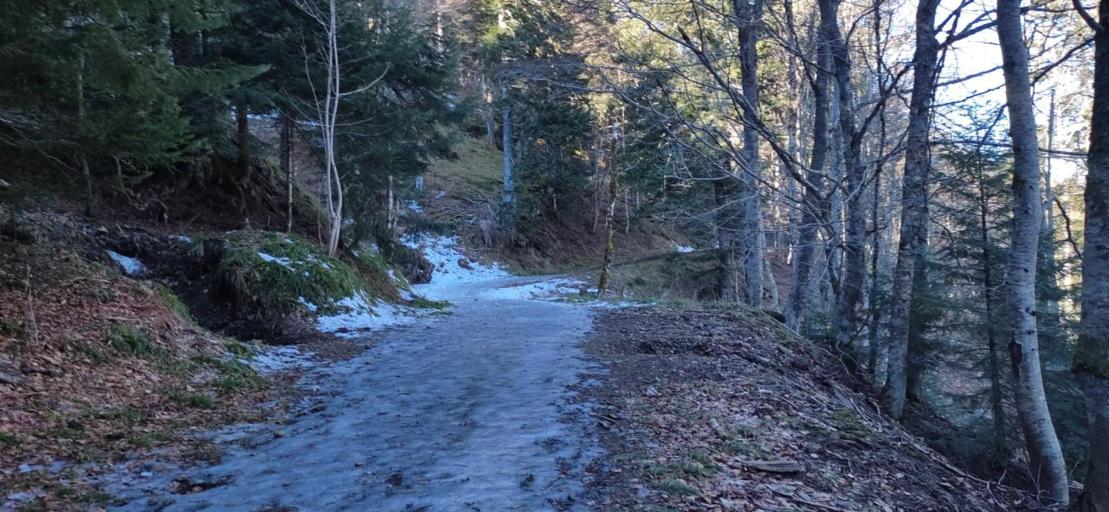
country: FR
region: Auvergne
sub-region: Departement du Puy-de-Dome
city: Mont-Dore
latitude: 45.5602
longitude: 2.8079
